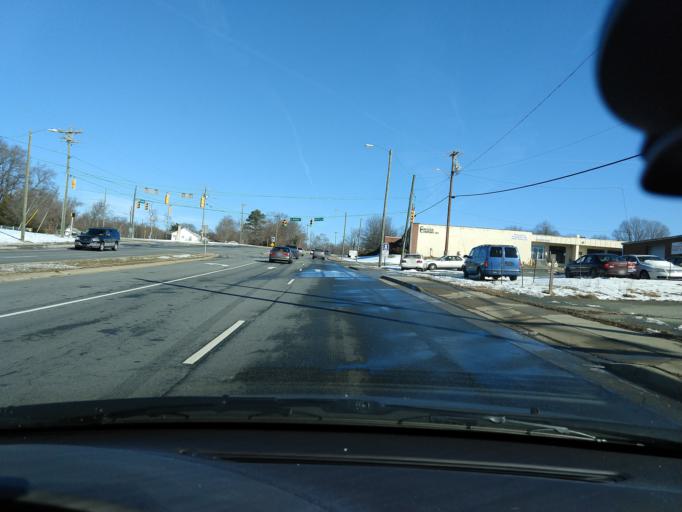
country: US
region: North Carolina
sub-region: Guilford County
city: Greensboro
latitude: 36.0468
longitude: -79.8111
